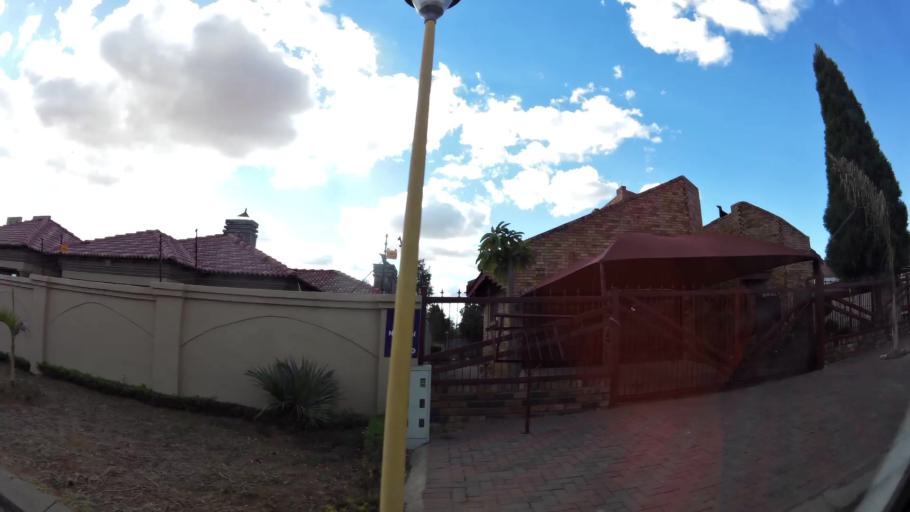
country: ZA
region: Limpopo
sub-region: Capricorn District Municipality
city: Polokwane
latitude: -23.9139
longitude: 29.5021
